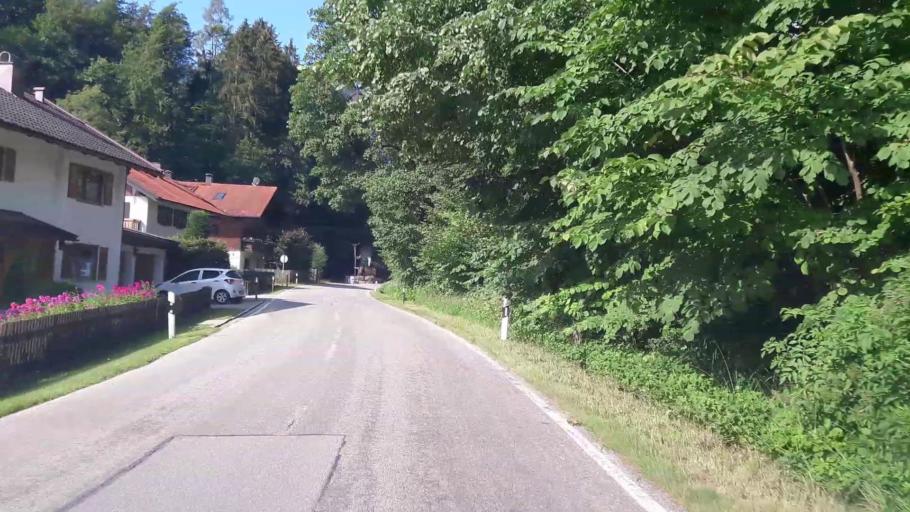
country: DE
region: Bavaria
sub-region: Upper Bavaria
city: Ruhpolding
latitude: 47.7415
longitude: 12.6132
